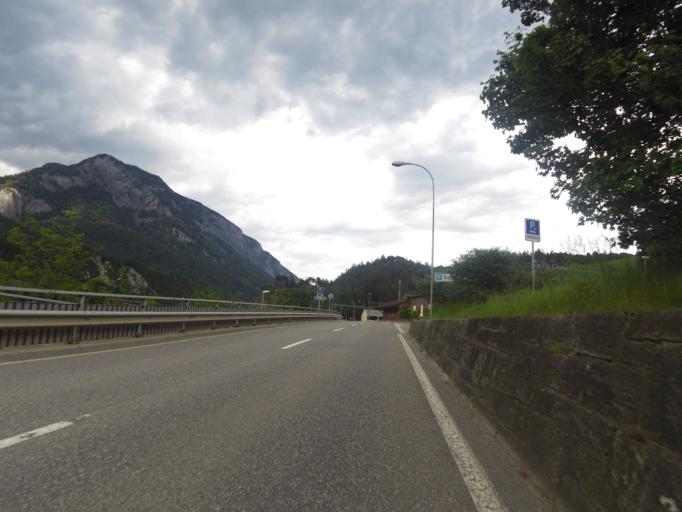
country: CH
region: Grisons
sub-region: Imboden District
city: Tamins
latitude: 46.8238
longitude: 9.4121
